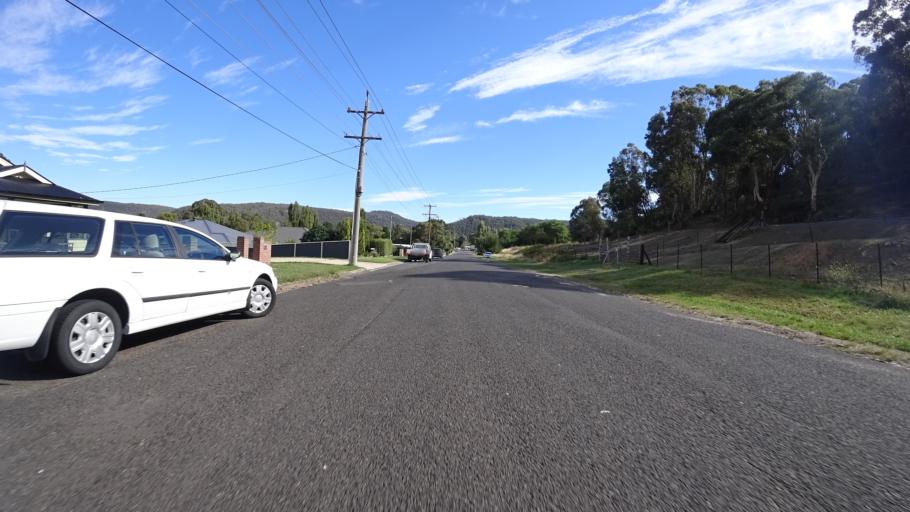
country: AU
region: New South Wales
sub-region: Lithgow
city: Lithgow
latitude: -33.4807
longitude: 150.1754
